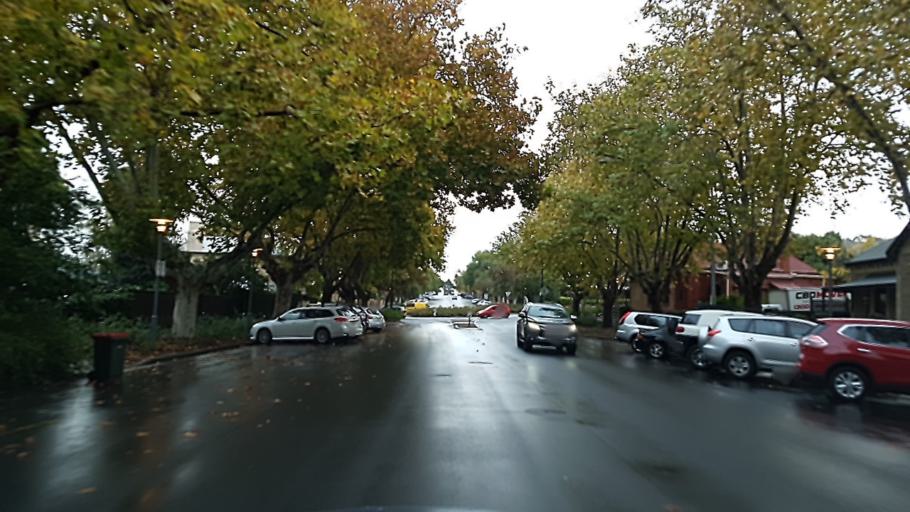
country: AU
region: South Australia
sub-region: Adelaide
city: North Adelaide
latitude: -34.9060
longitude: 138.6057
